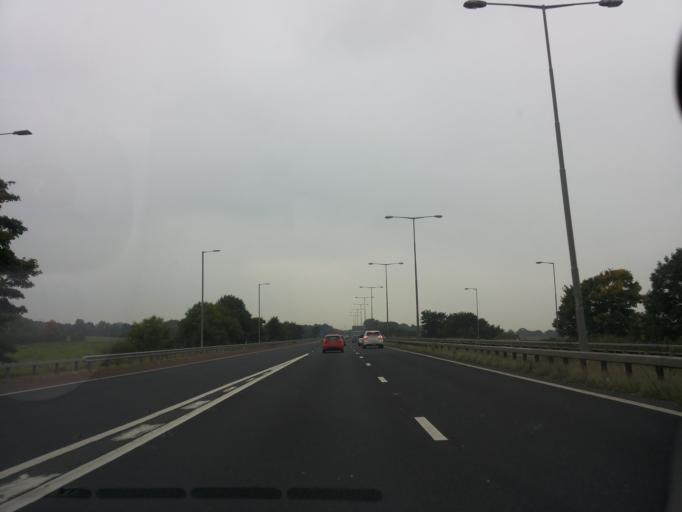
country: GB
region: England
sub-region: Lancashire
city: Preston
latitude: 53.8002
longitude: -2.7216
